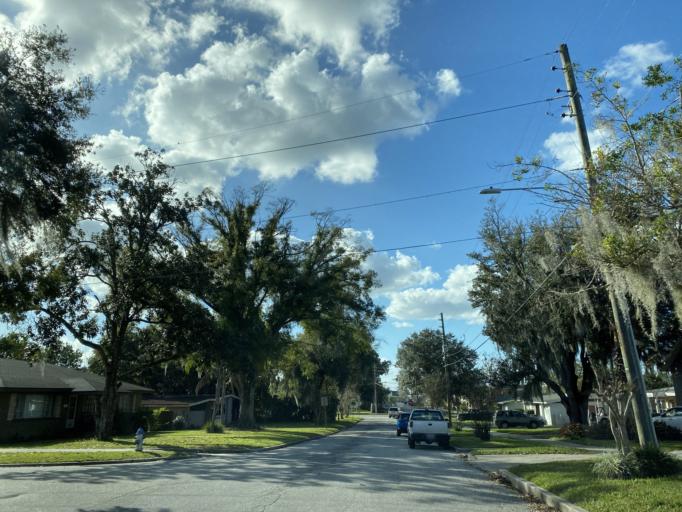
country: US
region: Florida
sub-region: Orange County
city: Orlando
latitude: 28.5518
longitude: -81.4045
